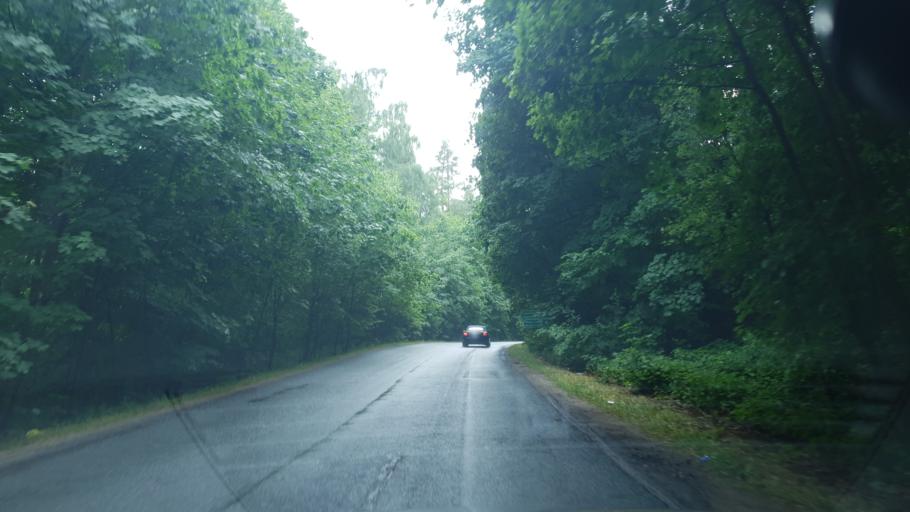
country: PL
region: Pomeranian Voivodeship
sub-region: Powiat kartuski
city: Chmielno
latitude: 54.2619
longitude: 18.0430
